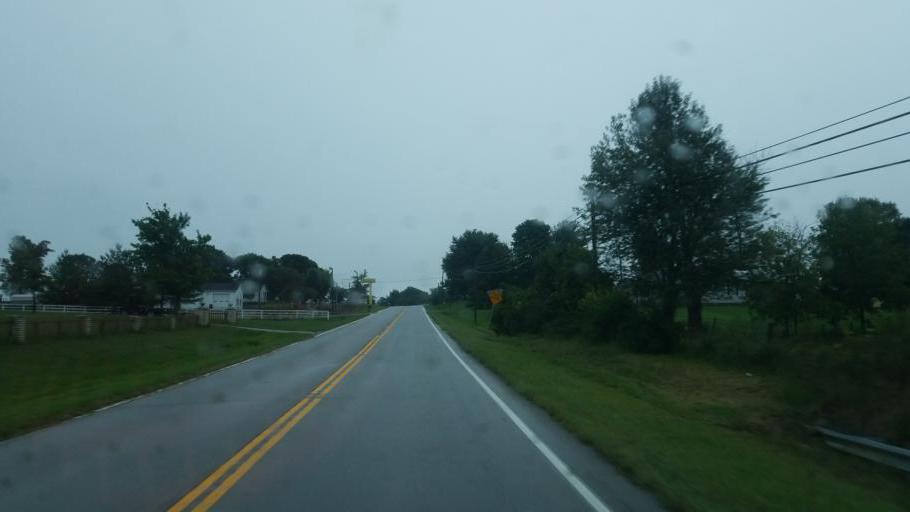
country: US
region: Kentucky
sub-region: Fleming County
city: Flemingsburg
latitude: 38.3918
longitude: -83.6873
